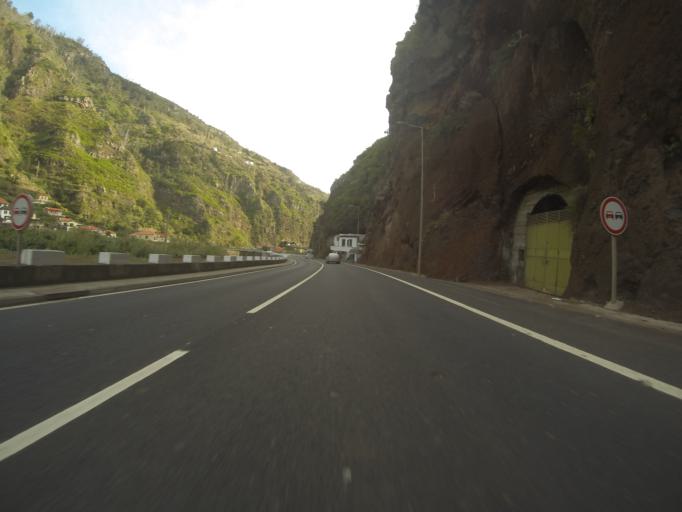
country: PT
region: Madeira
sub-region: Ribeira Brava
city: Campanario
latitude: 32.6887
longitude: -17.0508
